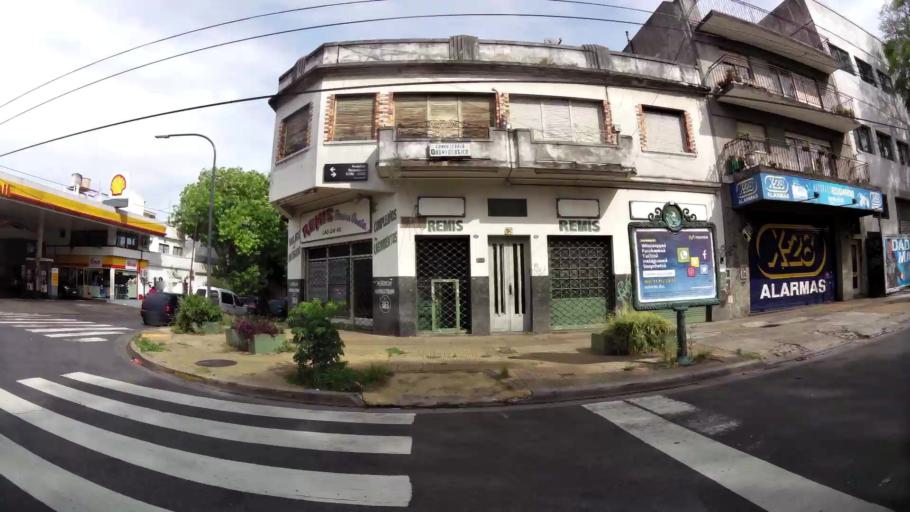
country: AR
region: Buenos Aires F.D.
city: Villa Lugano
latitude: -34.6555
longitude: -58.4967
